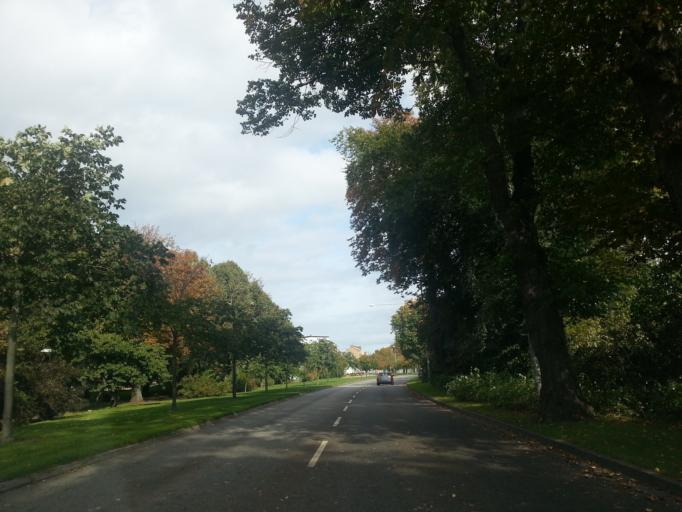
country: SE
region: Skane
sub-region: Landskrona
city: Landskrona
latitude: 55.8688
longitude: 12.8334
